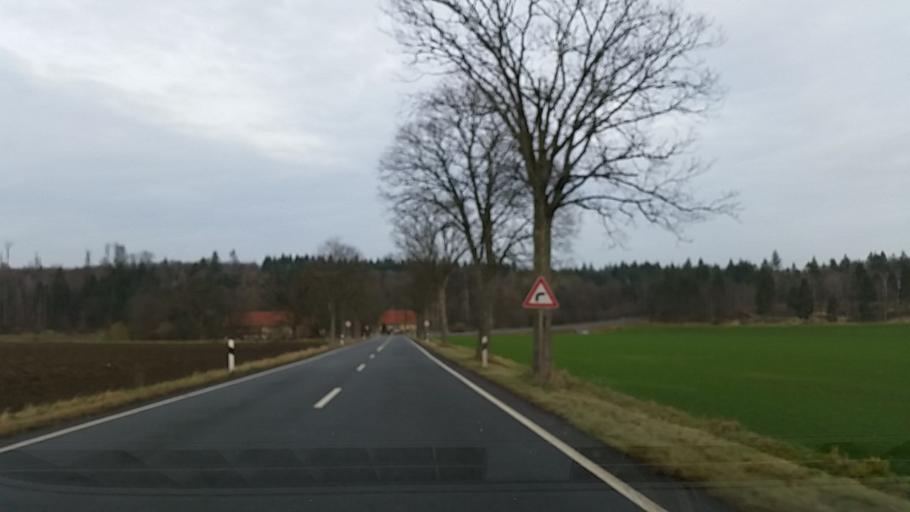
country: DE
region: Lower Saxony
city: Alt Wallmoden
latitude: 52.0088
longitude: 10.3041
